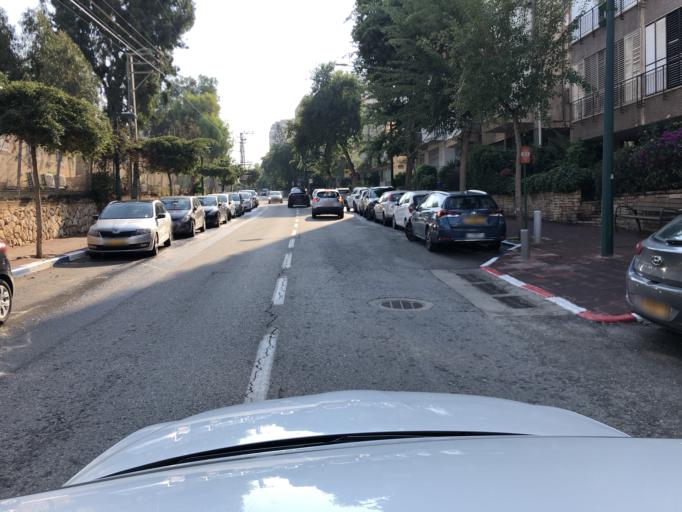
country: IL
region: Tel Aviv
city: Ramat Gan
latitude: 32.0878
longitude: 34.8203
